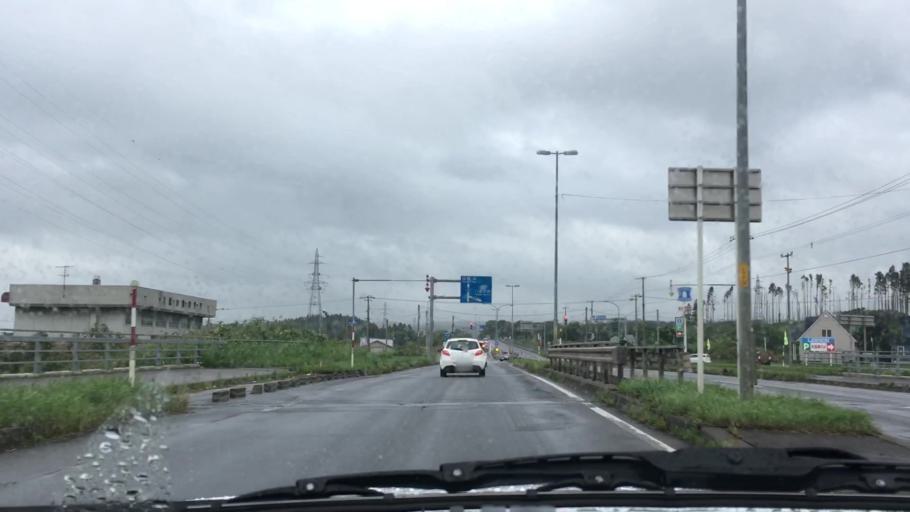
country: JP
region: Hokkaido
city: Nanae
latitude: 42.2469
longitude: 140.2888
